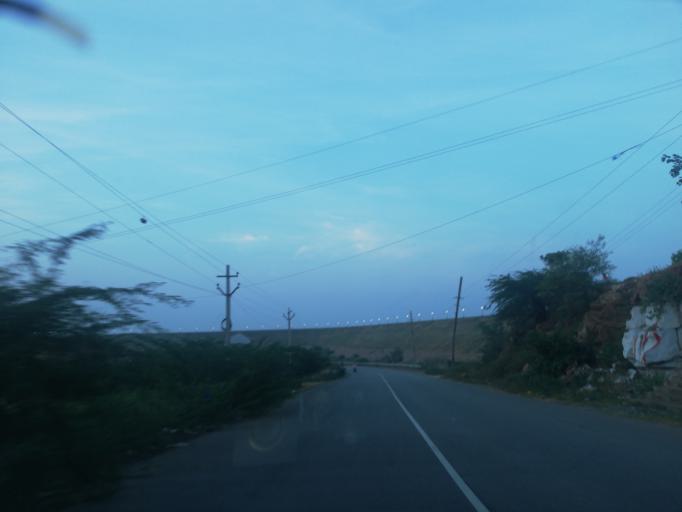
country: IN
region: Andhra Pradesh
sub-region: Guntur
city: Macherla
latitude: 16.5996
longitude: 79.3079
